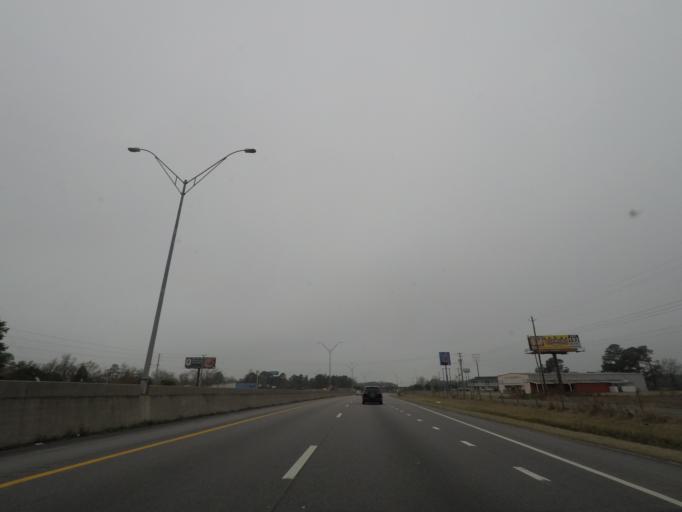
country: US
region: North Carolina
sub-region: Robeson County
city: Lumberton
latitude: 34.6367
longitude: -79.0214
